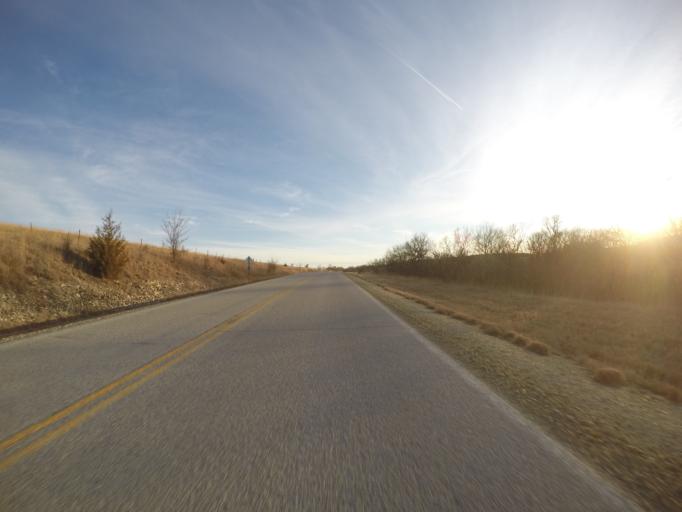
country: US
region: Kansas
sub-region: Riley County
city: Ogden
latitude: 39.3069
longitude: -96.7455
